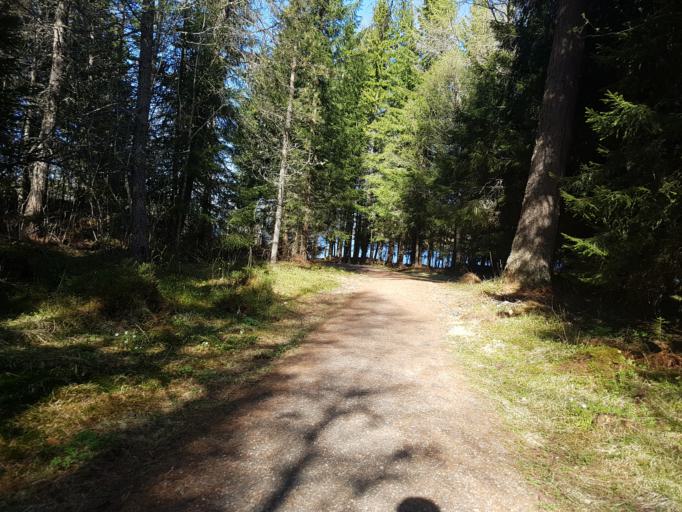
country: NO
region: Sor-Trondelag
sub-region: Trondheim
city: Trondheim
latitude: 63.4201
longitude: 10.3448
